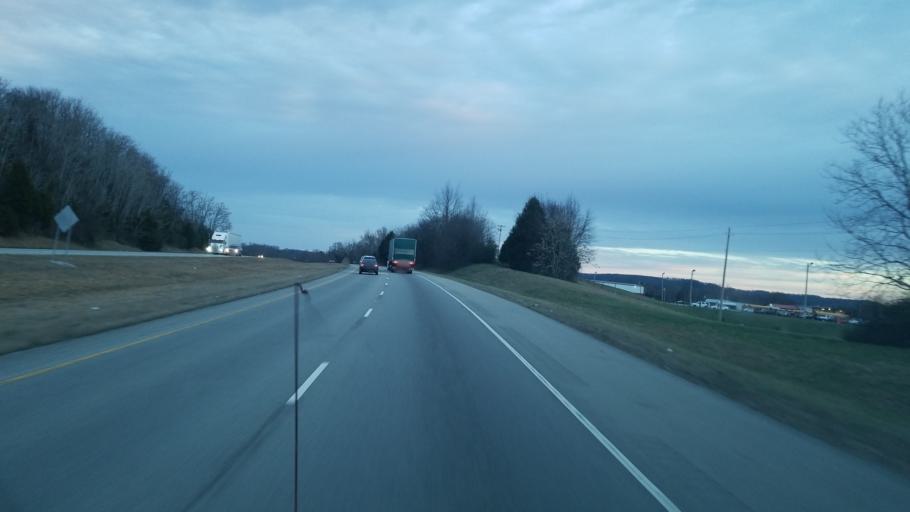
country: US
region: Tennessee
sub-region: White County
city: Sparta
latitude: 35.9478
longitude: -85.4834
